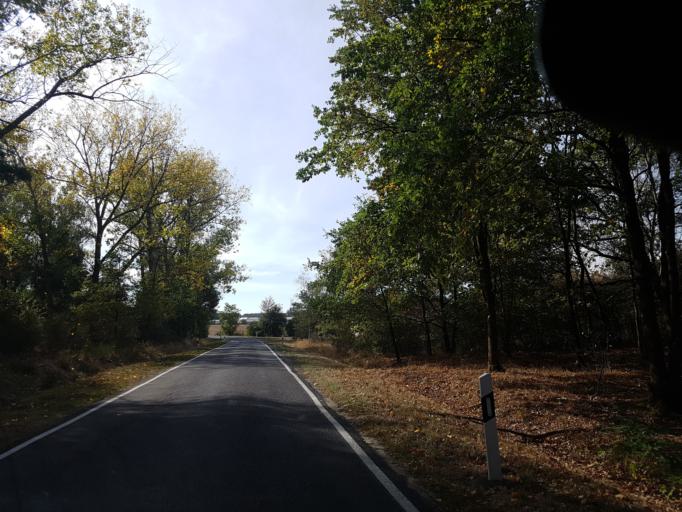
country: DE
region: Brandenburg
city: Schlieben
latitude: 51.7845
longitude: 13.3217
